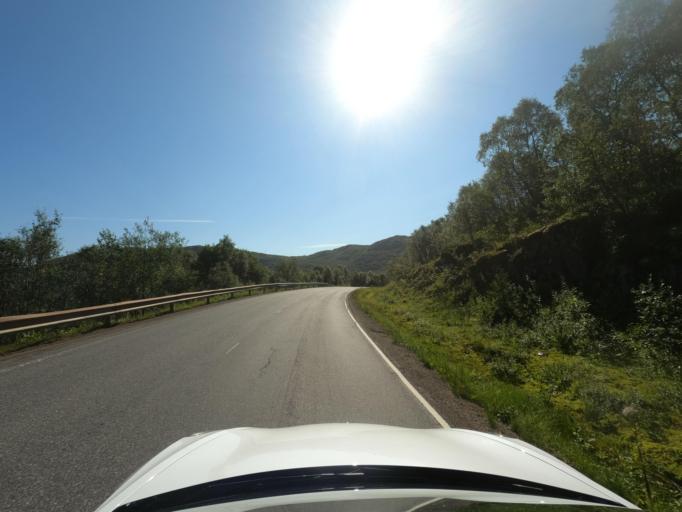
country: NO
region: Nordland
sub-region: Lodingen
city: Lodingen
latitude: 68.5544
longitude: 15.7501
